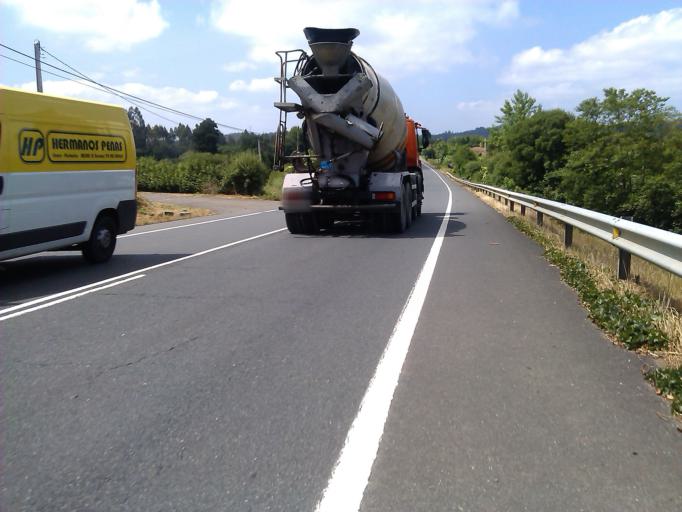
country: ES
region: Galicia
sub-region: Provincia da Coruna
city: Touro
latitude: 42.9214
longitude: -8.2983
